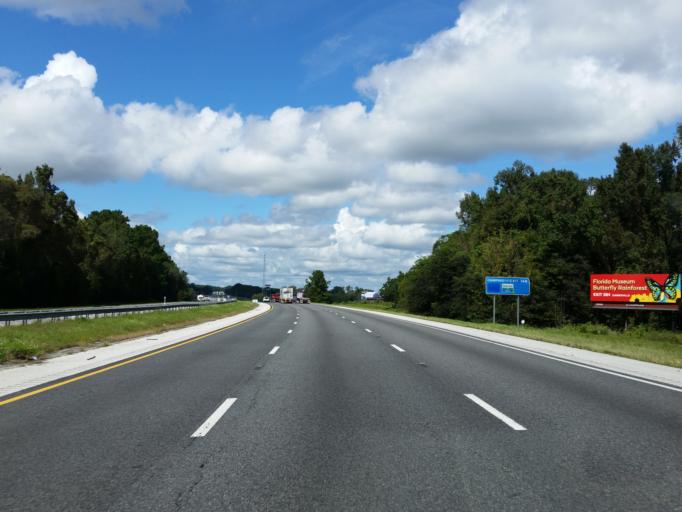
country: US
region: Florida
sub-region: Marion County
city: Citra
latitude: 29.3972
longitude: -82.2406
